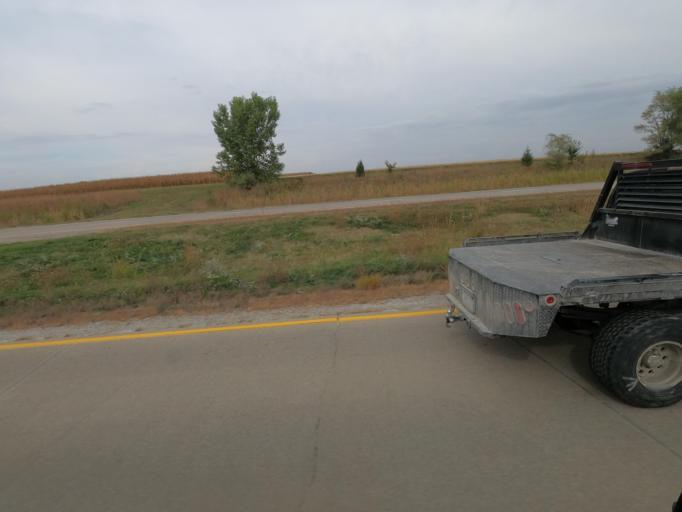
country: US
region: Iowa
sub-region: Marion County
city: Pella
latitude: 41.3895
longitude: -92.8427
